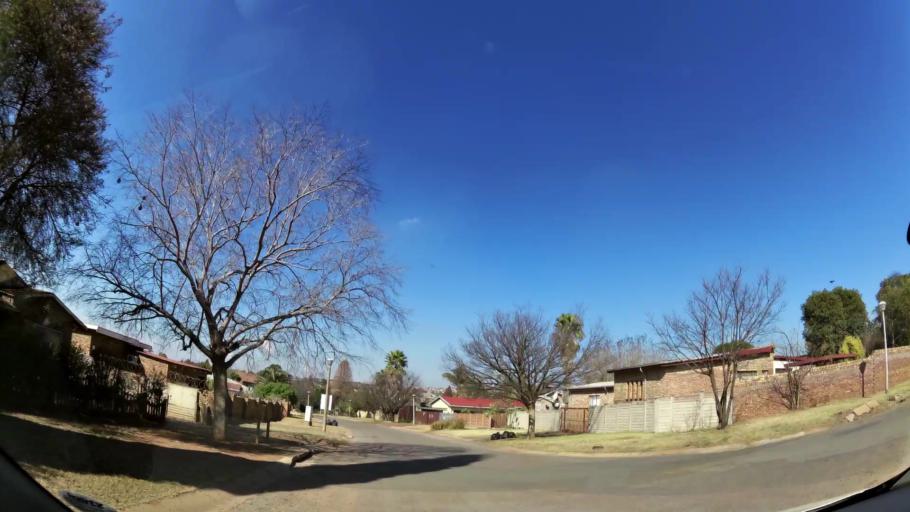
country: ZA
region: Mpumalanga
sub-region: Nkangala District Municipality
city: Witbank
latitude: -25.8452
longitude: 29.2457
